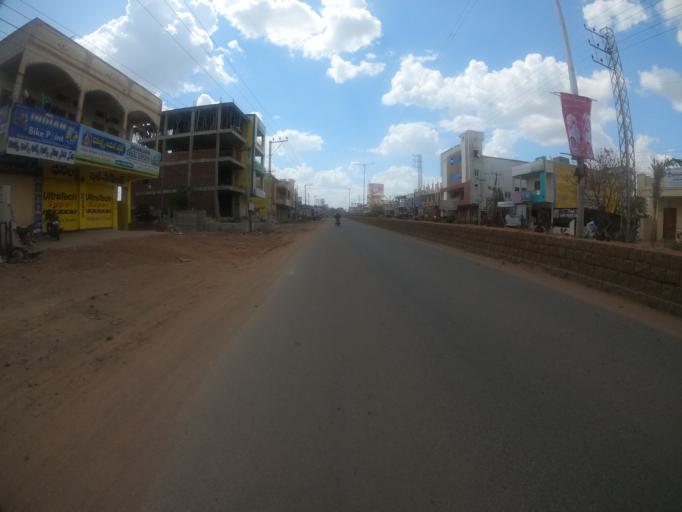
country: IN
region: Telangana
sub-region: Rangareddi
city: Sriramnagar
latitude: 17.3099
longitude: 78.1420
